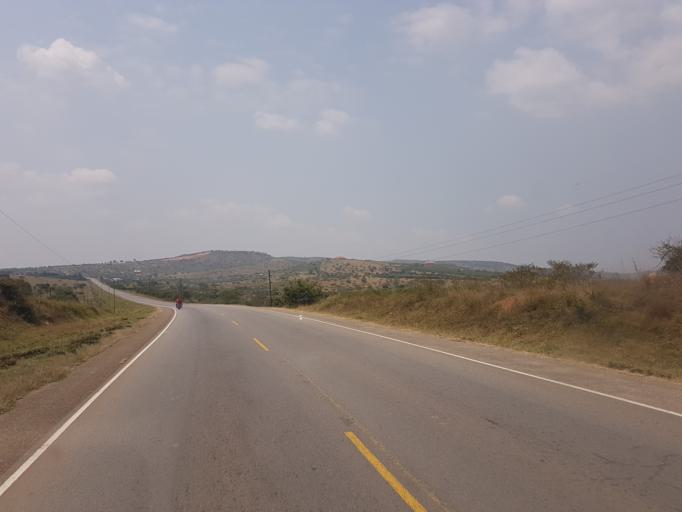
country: UG
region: Western Region
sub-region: Mbarara District
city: Mbarara
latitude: -0.5090
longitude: 30.8398
